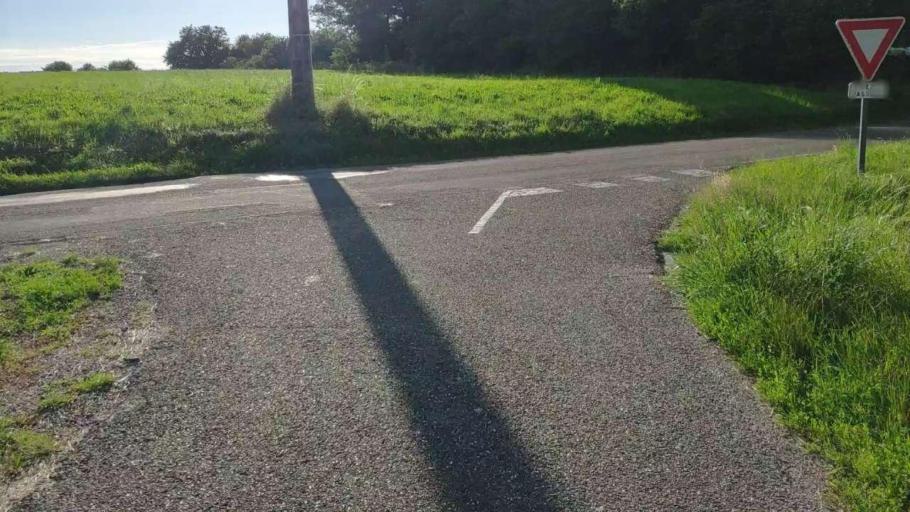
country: FR
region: Franche-Comte
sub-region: Departement du Jura
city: Bletterans
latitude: 46.7824
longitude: 5.4888
